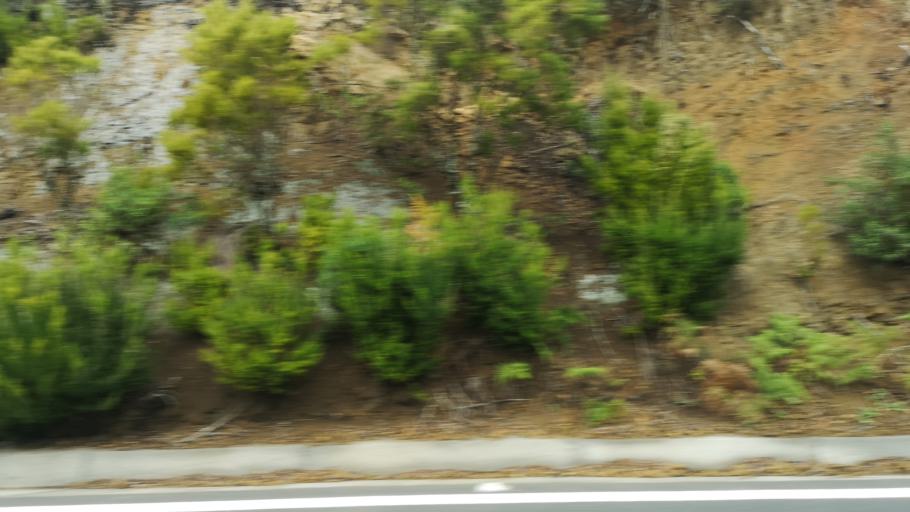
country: ES
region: Canary Islands
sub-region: Provincia de Santa Cruz de Tenerife
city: Vallehermosa
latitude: 28.1317
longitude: -17.2775
